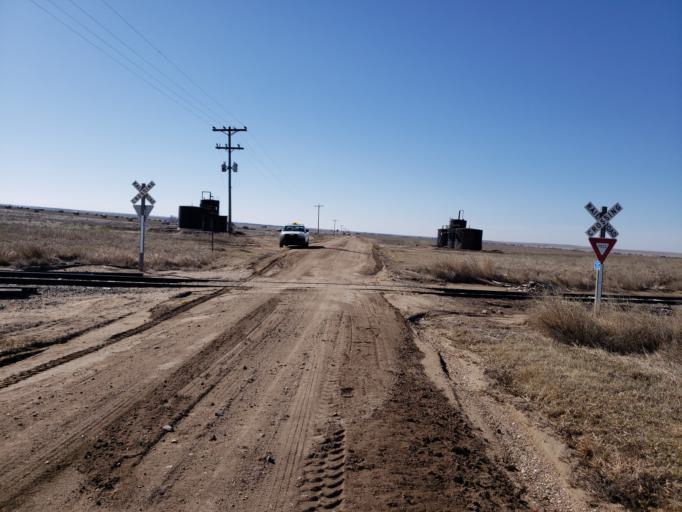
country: US
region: Kansas
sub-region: Ness County
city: Ness City
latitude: 38.4482
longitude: -100.0454
